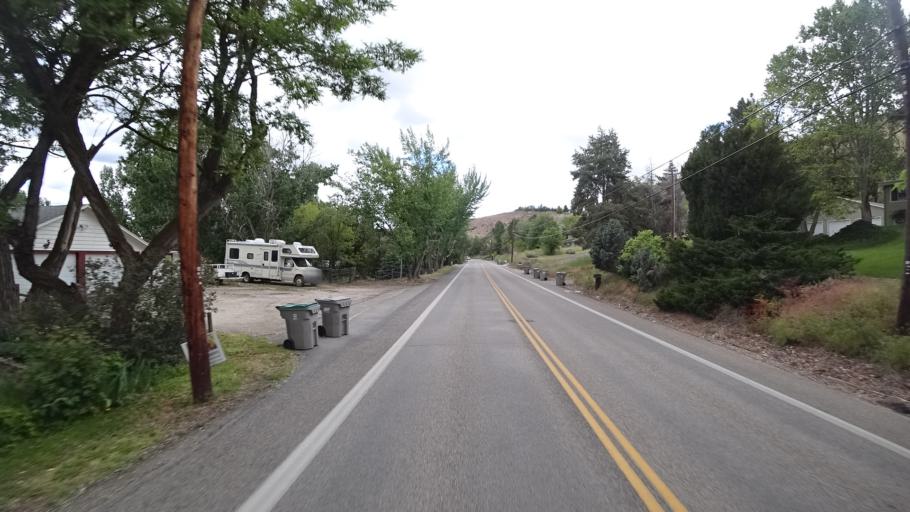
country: US
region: Idaho
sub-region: Ada County
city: Garden City
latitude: 43.6709
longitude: -116.2554
